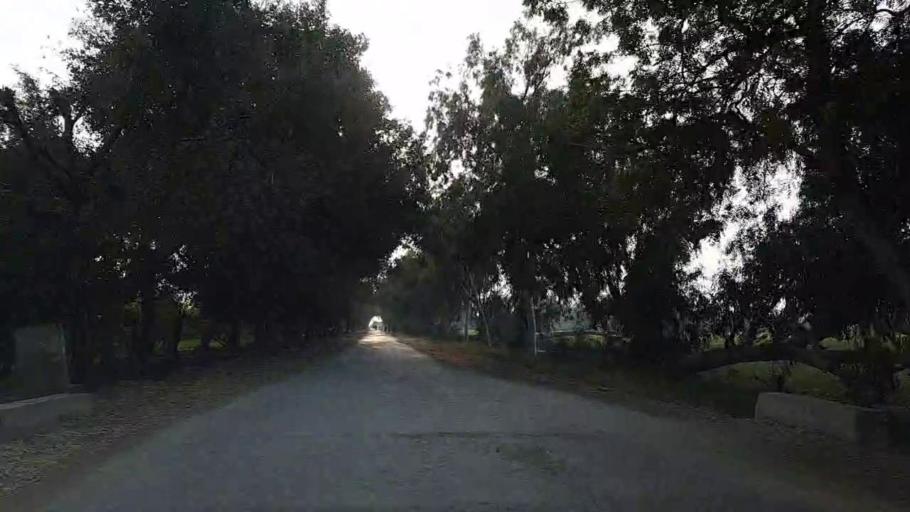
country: PK
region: Sindh
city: Mirwah Gorchani
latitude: 25.3091
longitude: 69.2132
